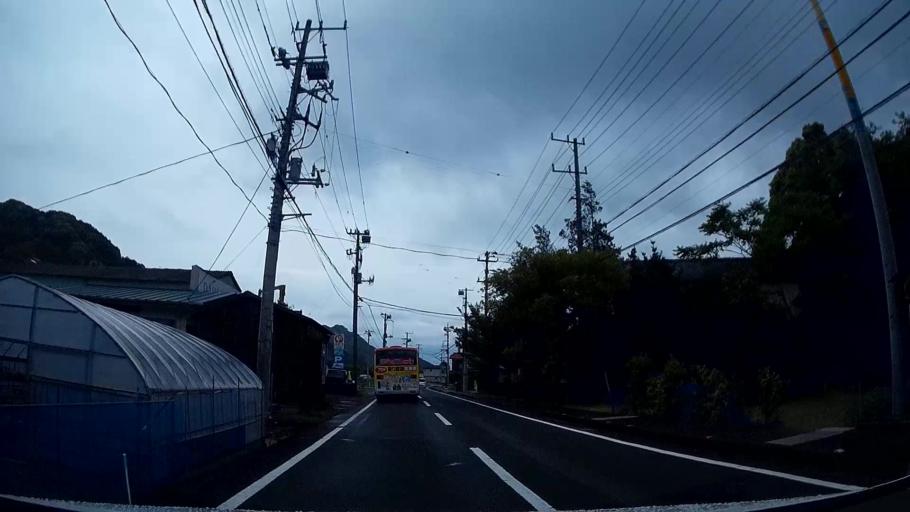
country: JP
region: Shizuoka
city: Shimoda
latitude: 34.7625
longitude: 138.9806
